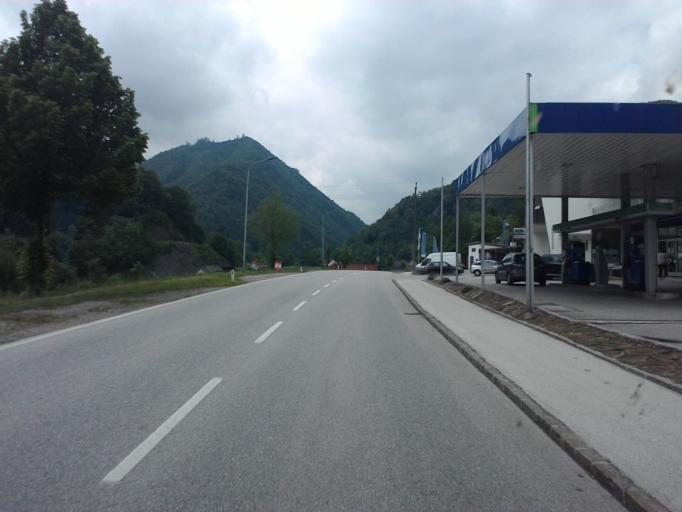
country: AT
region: Upper Austria
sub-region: Politischer Bezirk Steyr-Land
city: Maria Neustift
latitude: 47.8832
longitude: 14.5437
